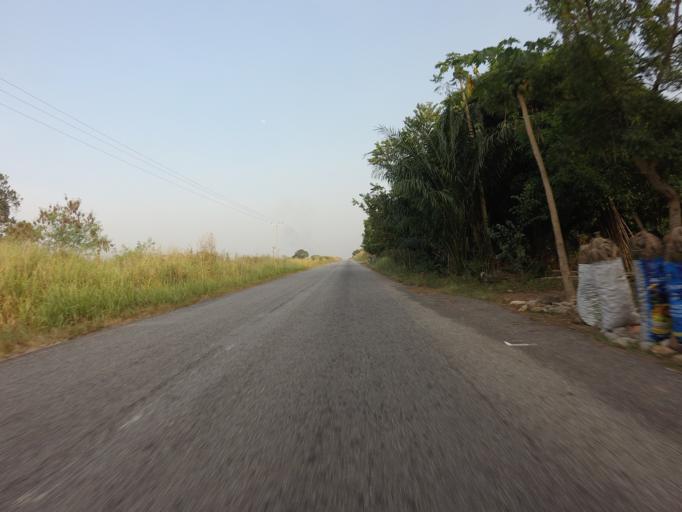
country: GH
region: Volta
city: Ho
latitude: 6.5736
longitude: 0.3519
